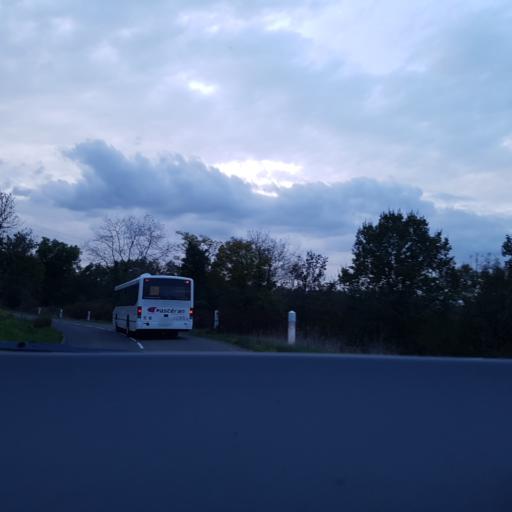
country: FR
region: Midi-Pyrenees
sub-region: Departement du Gers
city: Condom
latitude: 43.9510
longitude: 0.3111
